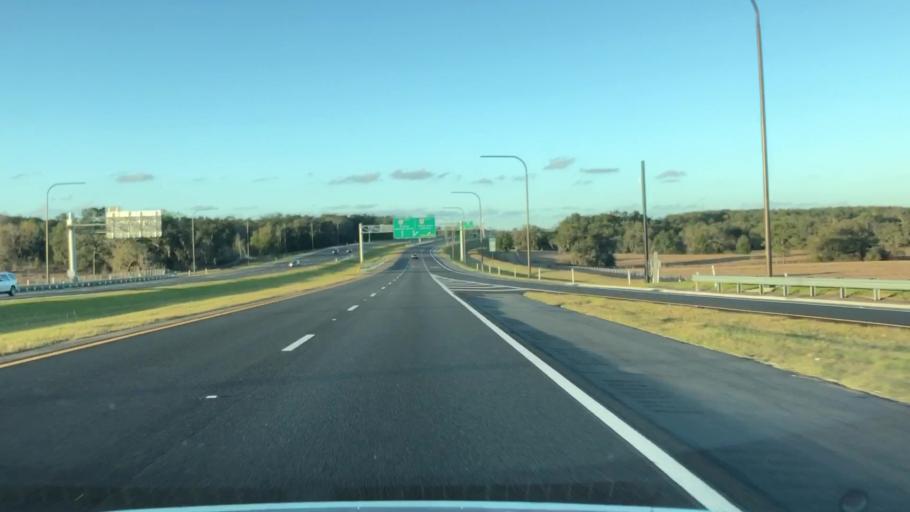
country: US
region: Florida
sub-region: Orange County
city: Zellwood
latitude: 28.7605
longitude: -81.5669
